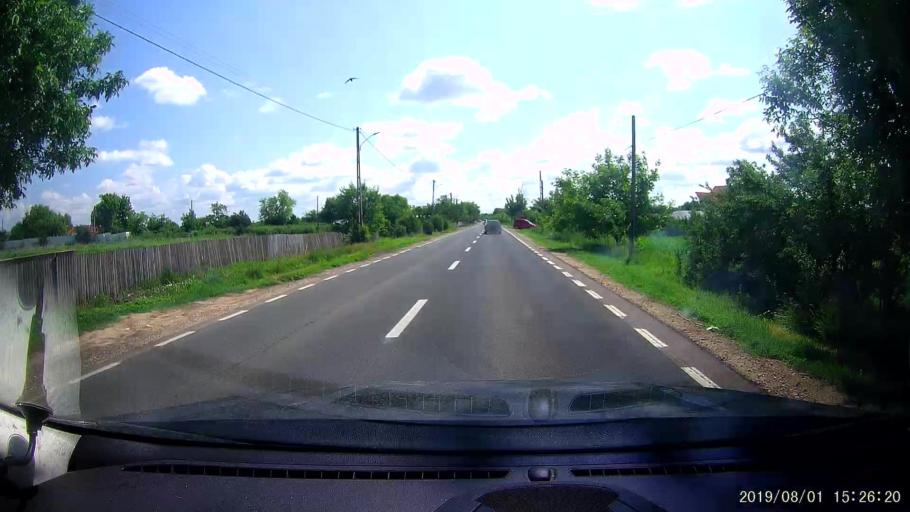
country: RO
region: Braila
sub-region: Comuna Viziru
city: Viziru
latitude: 45.0107
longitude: 27.7222
